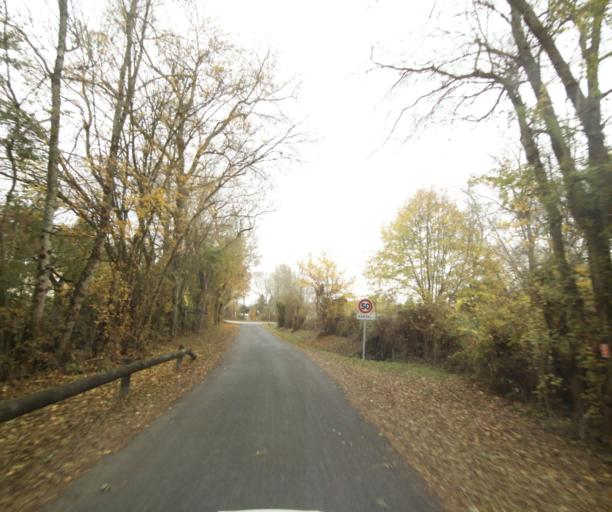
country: FR
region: Poitou-Charentes
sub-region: Departement de la Charente-Maritime
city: Saintes
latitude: 45.7610
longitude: -0.6268
